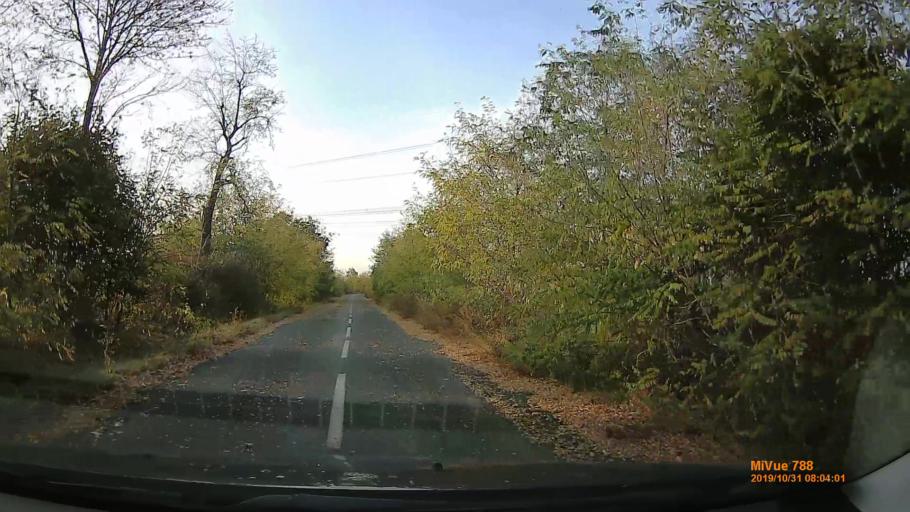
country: HU
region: Pest
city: Pilis
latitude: 47.3153
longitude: 19.5659
